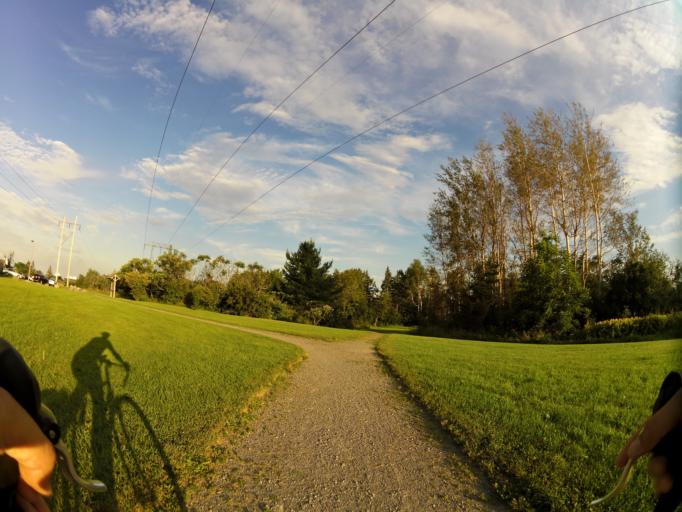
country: CA
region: Ontario
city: Bells Corners
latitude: 45.3357
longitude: -75.9150
